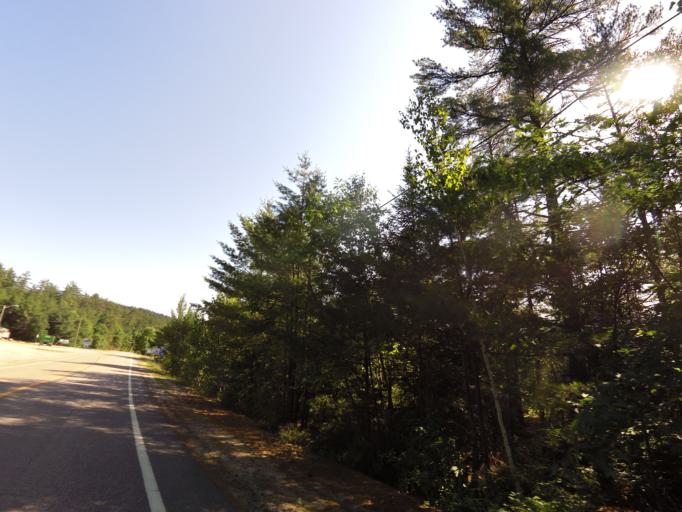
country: CA
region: Ontario
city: Deep River
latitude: 46.1934
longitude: -77.6849
